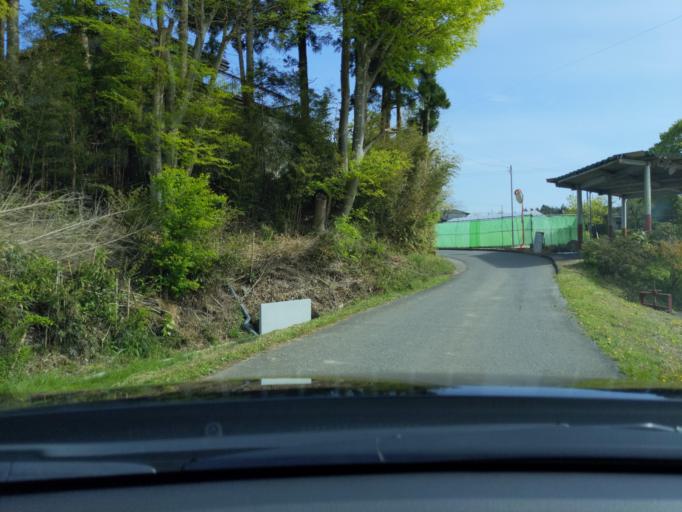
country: JP
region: Fukushima
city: Koriyama
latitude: 37.3624
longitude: 140.4174
